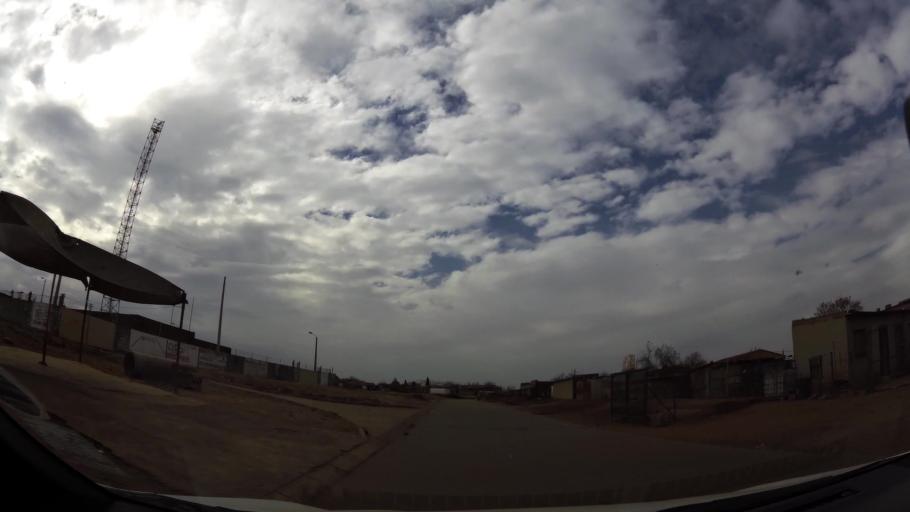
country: ZA
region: Gauteng
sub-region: Ekurhuleni Metropolitan Municipality
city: Germiston
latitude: -26.3994
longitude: 28.1486
